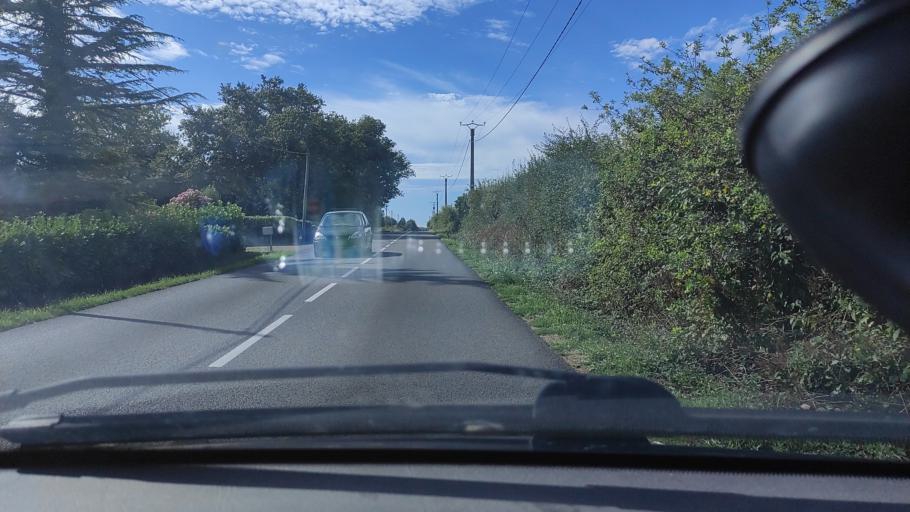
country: FR
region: Pays de la Loire
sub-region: Departement de la Vendee
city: La Boissiere-des-Landes
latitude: 46.5544
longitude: -1.4328
